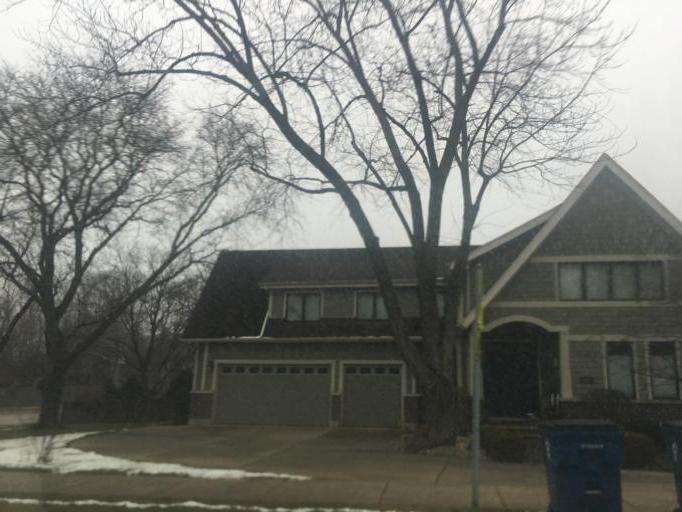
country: US
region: Illinois
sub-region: DuPage County
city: Downers Grove
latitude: 41.7870
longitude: -88.0187
